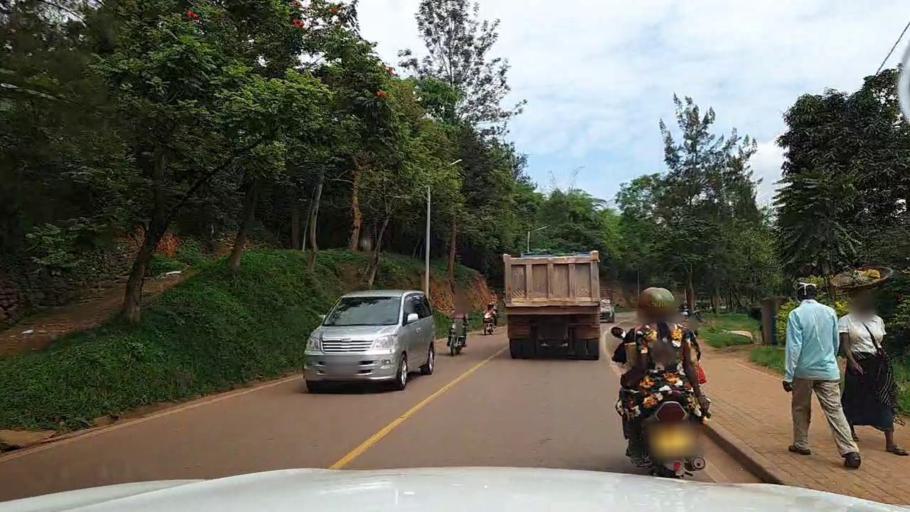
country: RW
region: Kigali
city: Kigali
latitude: -1.9167
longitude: 30.0474
